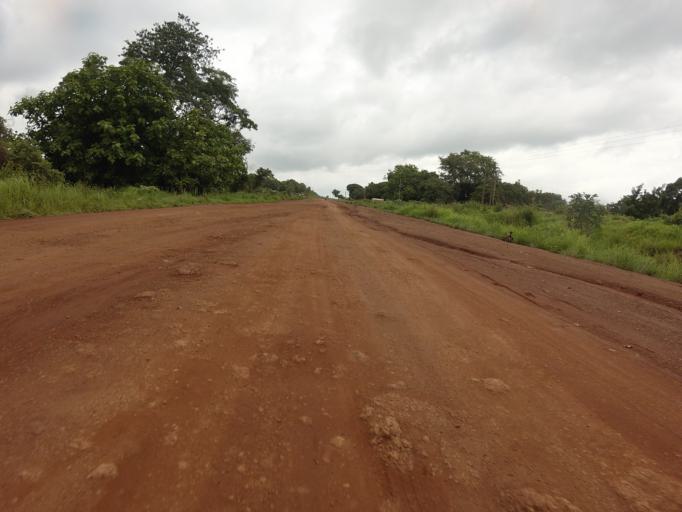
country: GH
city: Kpandae
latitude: 8.3144
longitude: 0.4801
